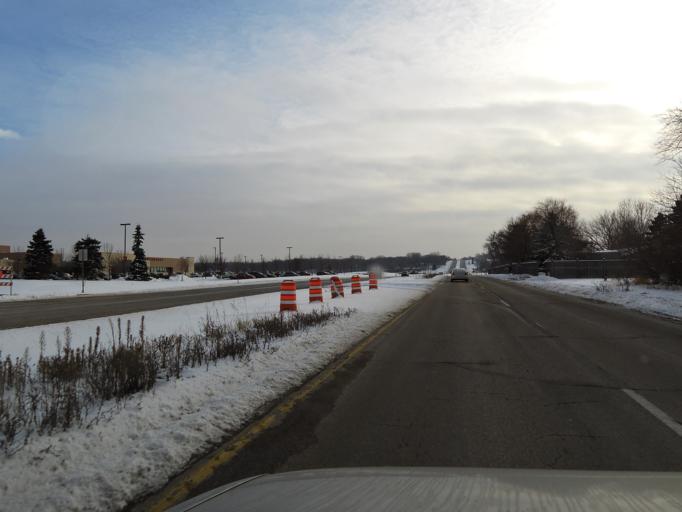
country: US
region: Minnesota
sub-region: Scott County
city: Shakopee
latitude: 44.7730
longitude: -93.5056
